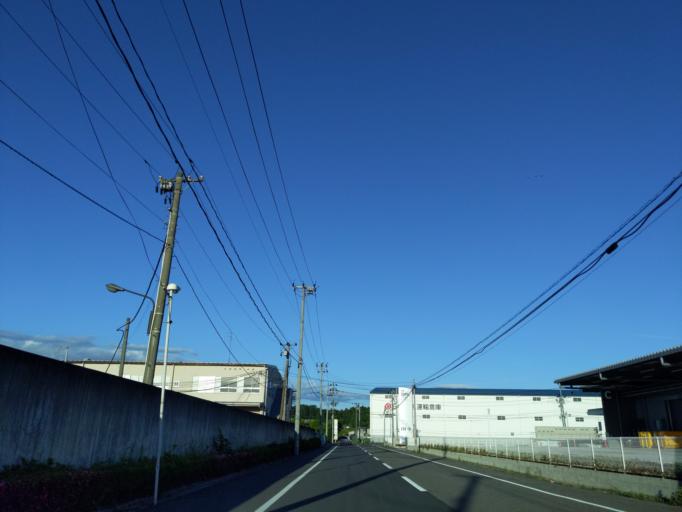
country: JP
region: Fukushima
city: Koriyama
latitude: 37.3775
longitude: 140.4024
